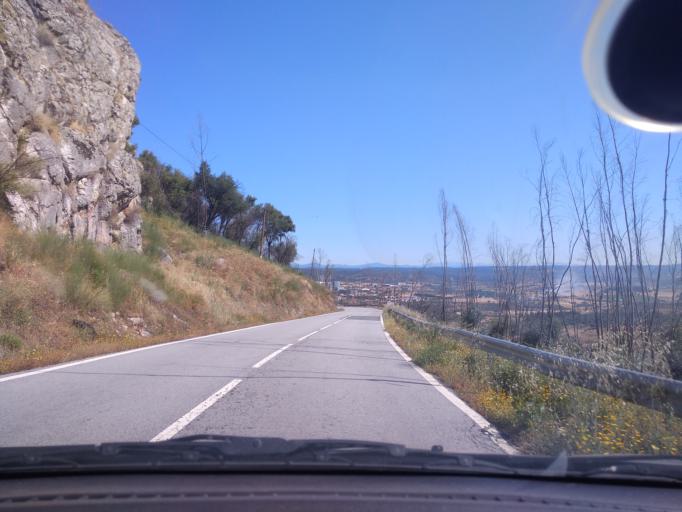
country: PT
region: Portalegre
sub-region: Nisa
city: Nisa
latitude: 39.6301
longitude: -7.6634
